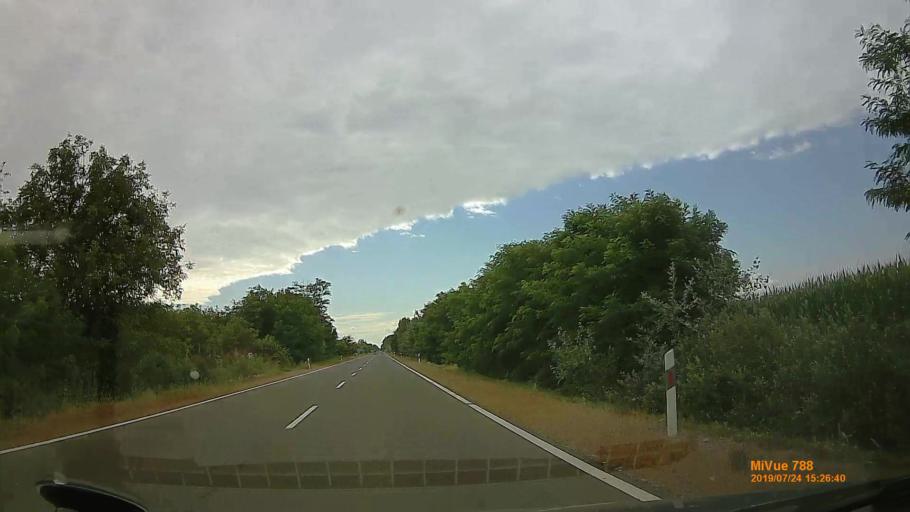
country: HU
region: Szabolcs-Szatmar-Bereg
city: Tarpa
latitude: 48.1602
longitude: 22.5191
